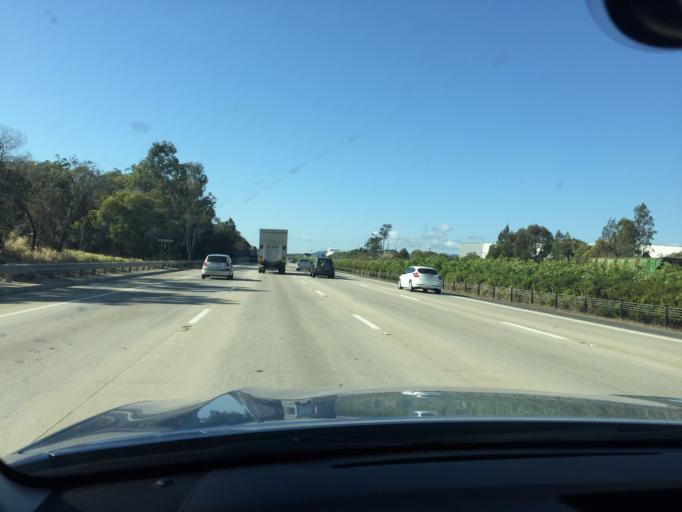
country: AU
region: Queensland
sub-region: Gold Coast
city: Yatala
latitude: -27.7433
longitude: 153.2328
